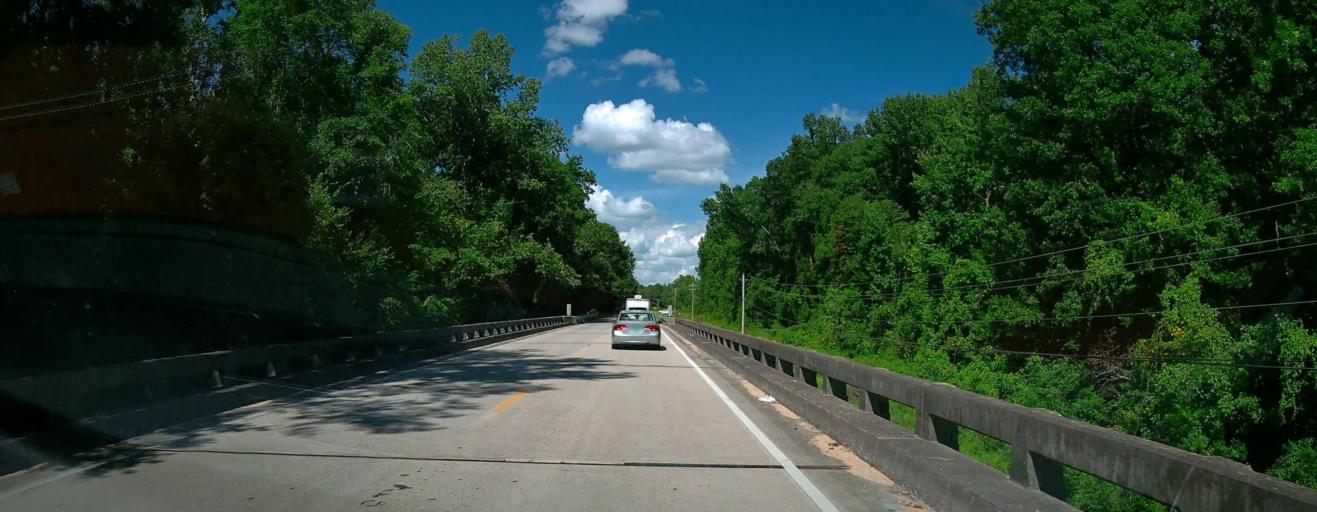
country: US
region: Alabama
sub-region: Macon County
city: Tuskegee
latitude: 32.3801
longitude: -85.8282
